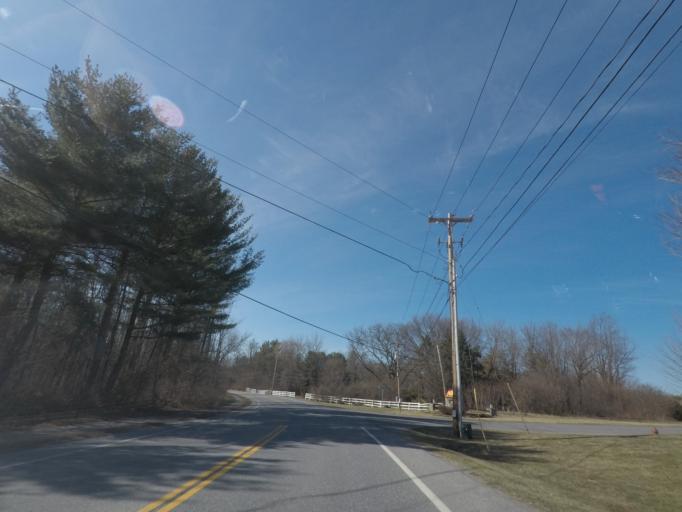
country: US
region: New York
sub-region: Saratoga County
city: Ballston Spa
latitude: 43.0001
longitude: -73.8273
